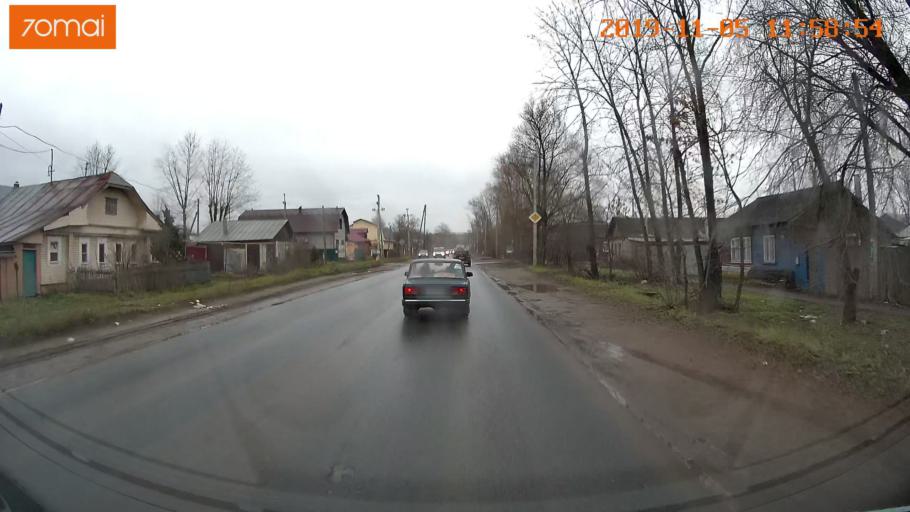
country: RU
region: Ivanovo
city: Kokhma
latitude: 56.9799
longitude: 41.0433
